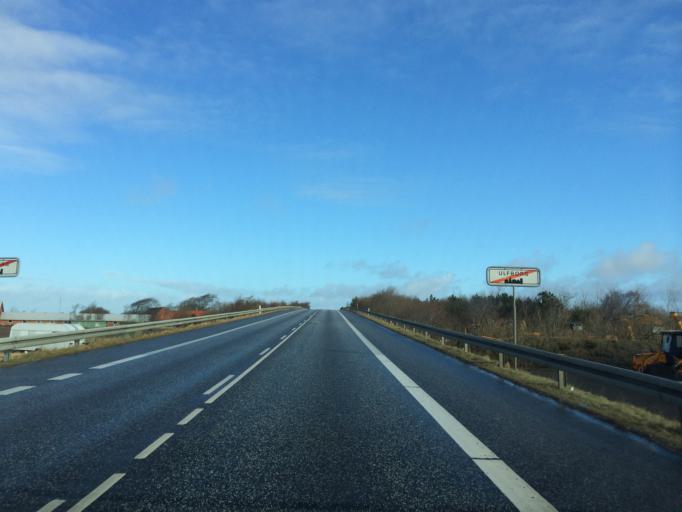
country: DK
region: Central Jutland
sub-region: Holstebro Kommune
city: Ulfborg
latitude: 56.2776
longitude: 8.3254
